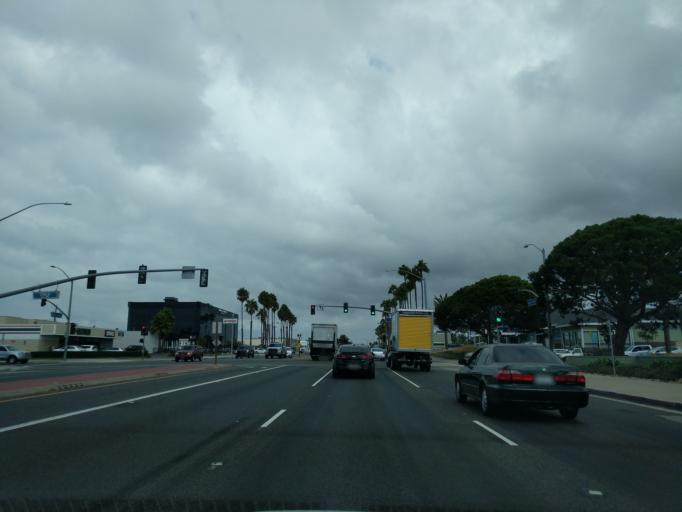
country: US
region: California
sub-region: Orange County
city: Huntington Beach
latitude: 33.6754
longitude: -117.9885
